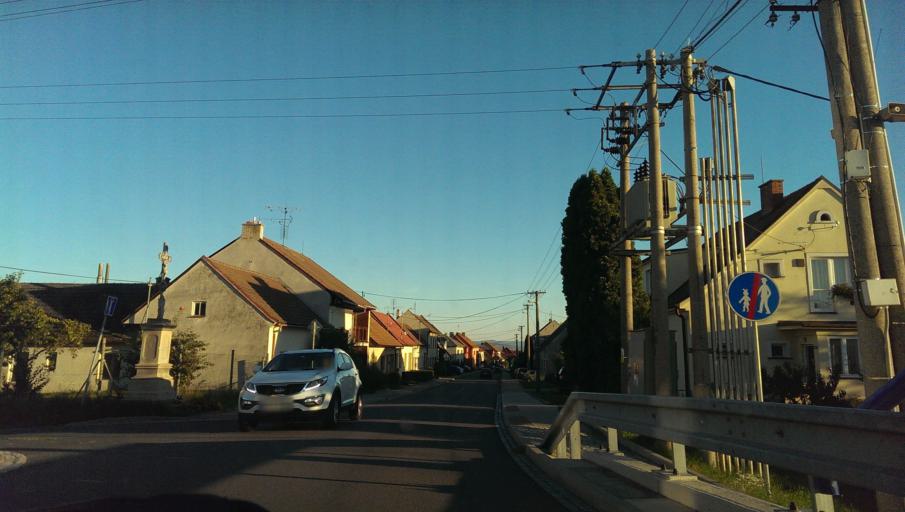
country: CZ
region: Zlin
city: Tupesy
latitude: 49.0834
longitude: 17.3744
